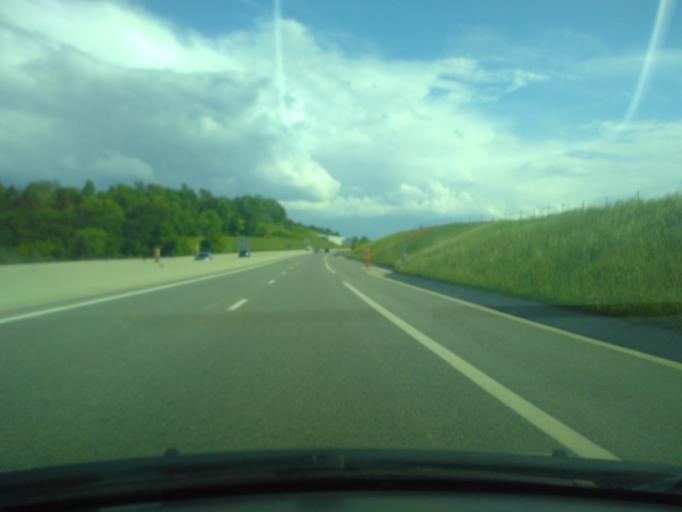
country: FR
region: Rhone-Alpes
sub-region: Departement de la Haute-Savoie
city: Allonzier-la-Caille
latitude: 46.0080
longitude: 6.1254
